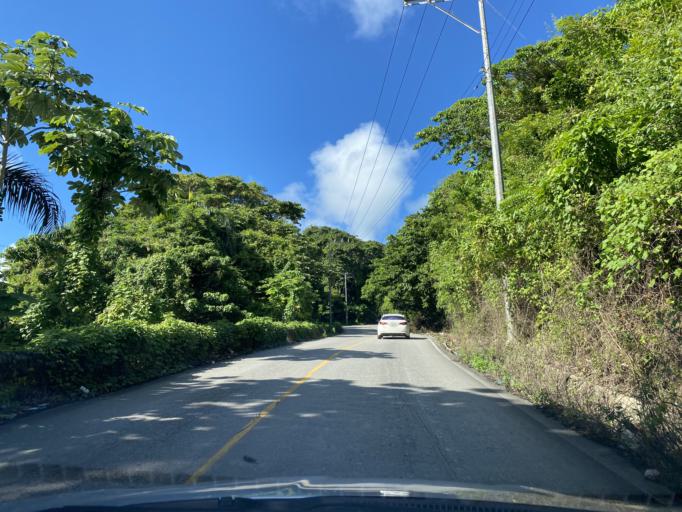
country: DO
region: Samana
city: Sanchez
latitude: 19.2380
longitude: -69.5975
